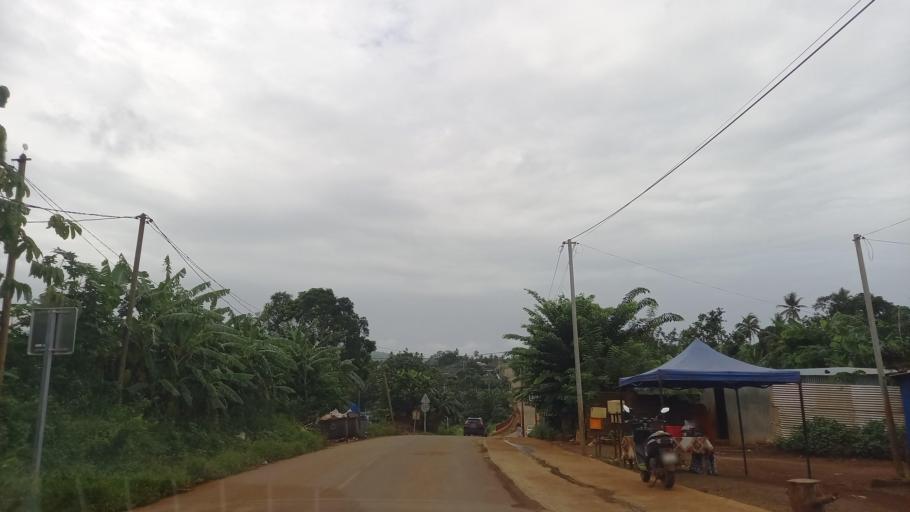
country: YT
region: Chiconi
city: Chiconi
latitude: -12.8241
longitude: 45.1296
